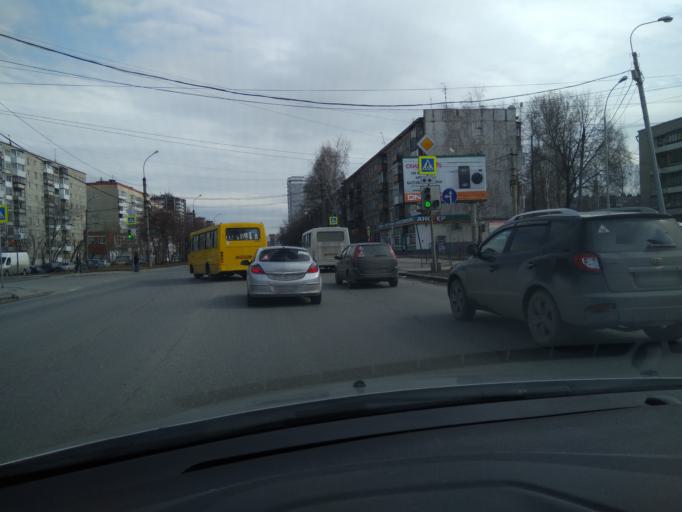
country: RU
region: Sverdlovsk
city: Shuvakish
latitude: 56.8658
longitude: 60.5330
